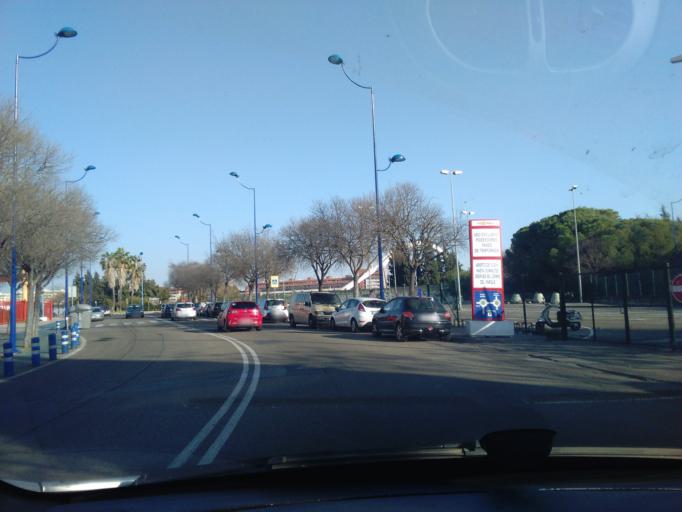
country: ES
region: Andalusia
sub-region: Provincia de Sevilla
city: Camas
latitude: 37.4051
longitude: -6.0004
